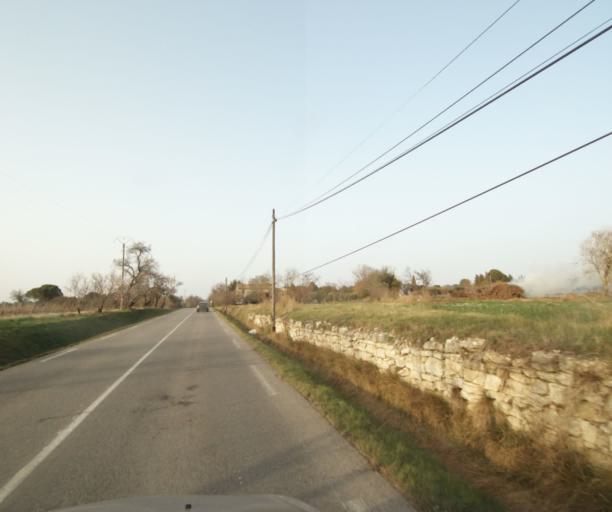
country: FR
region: Provence-Alpes-Cote d'Azur
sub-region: Departement des Bouches-du-Rhone
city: Eguilles
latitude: 43.5951
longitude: 5.3665
